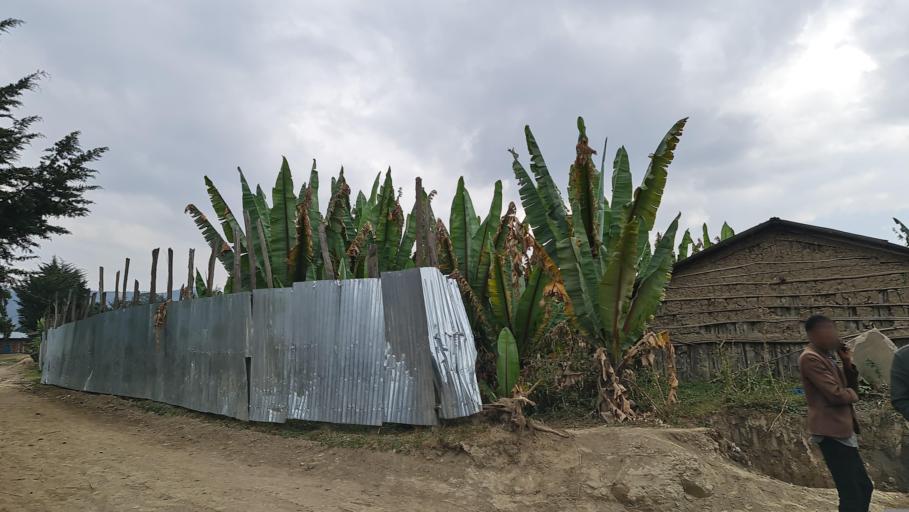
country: ET
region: Oromiya
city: Hagere Hiywet
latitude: 8.7996
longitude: 37.8851
